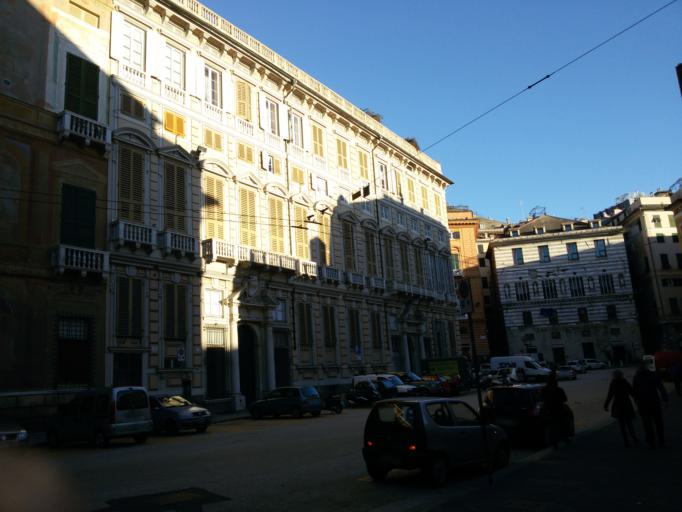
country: IT
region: Liguria
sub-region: Provincia di Genova
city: San Teodoro
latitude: 44.4107
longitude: 8.9346
